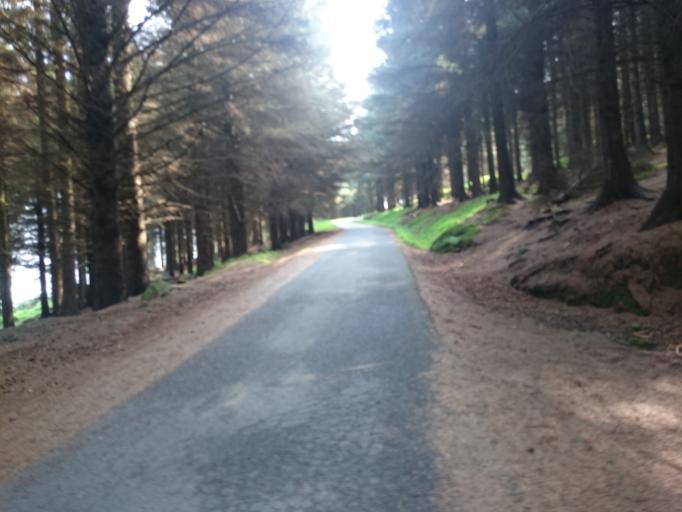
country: IE
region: Leinster
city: Ballinteer
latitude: 53.2537
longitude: -6.2445
